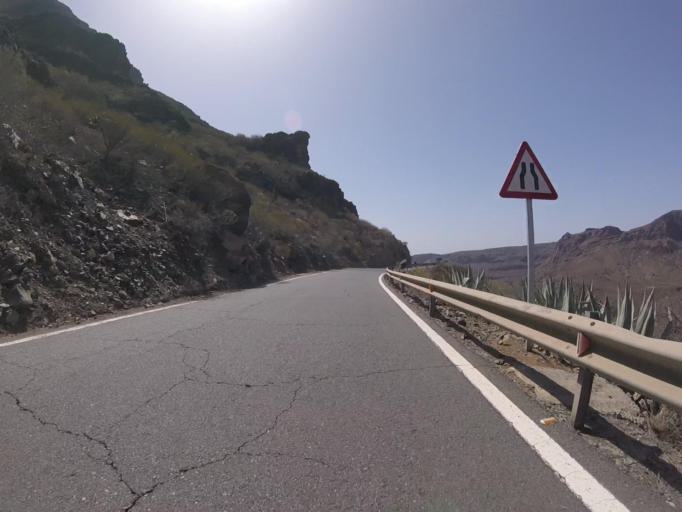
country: ES
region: Canary Islands
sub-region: Provincia de Las Palmas
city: Maspalomas
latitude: 27.8288
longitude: -15.5743
